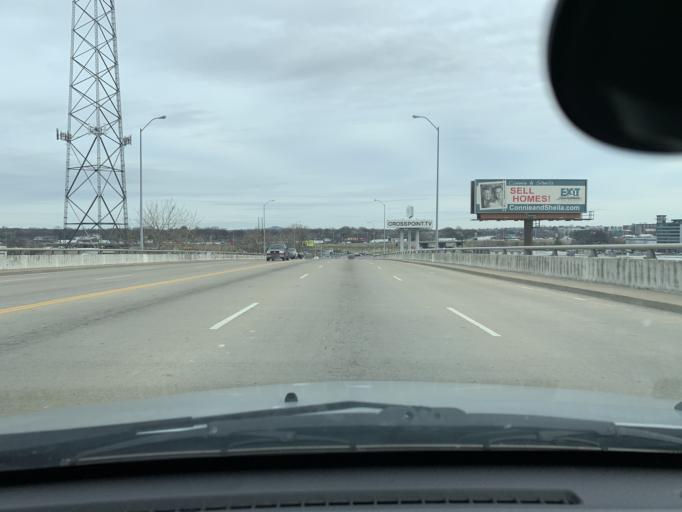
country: US
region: Tennessee
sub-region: Davidson County
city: Nashville
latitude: 36.1762
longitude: -86.7792
